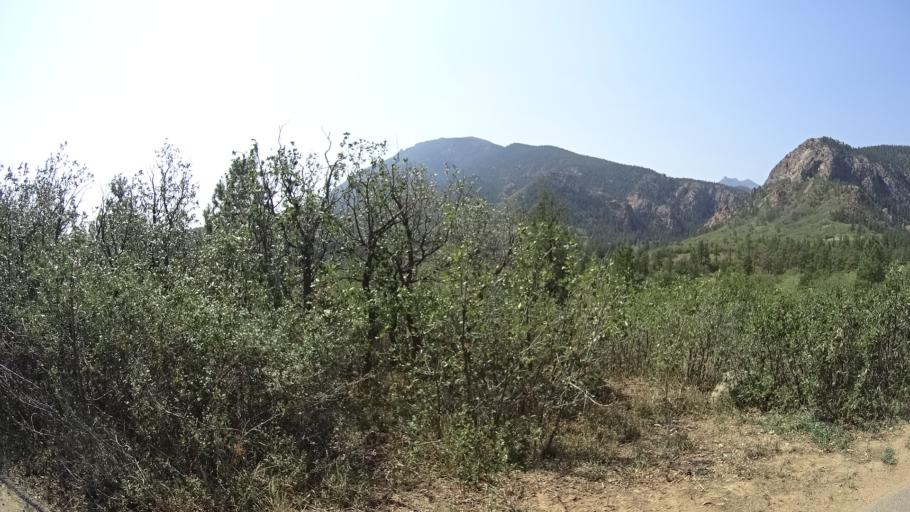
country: US
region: Colorado
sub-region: El Paso County
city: Colorado Springs
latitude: 38.7923
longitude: -104.8651
